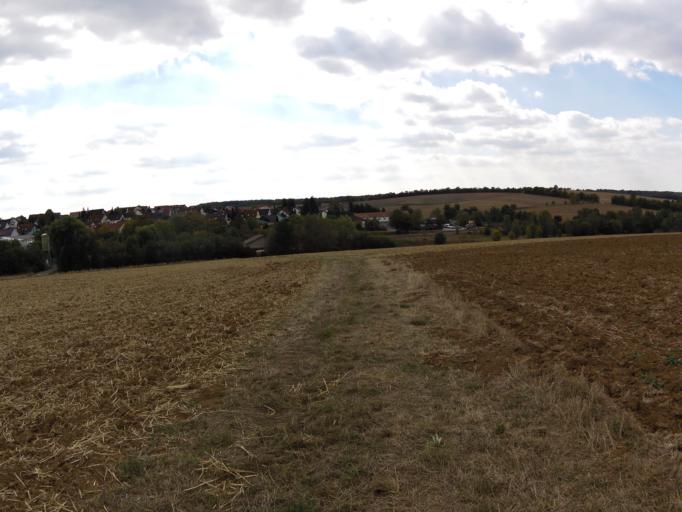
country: DE
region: Bavaria
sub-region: Regierungsbezirk Unterfranken
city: Waldbuttelbrunn
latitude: 49.7890
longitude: 9.8300
